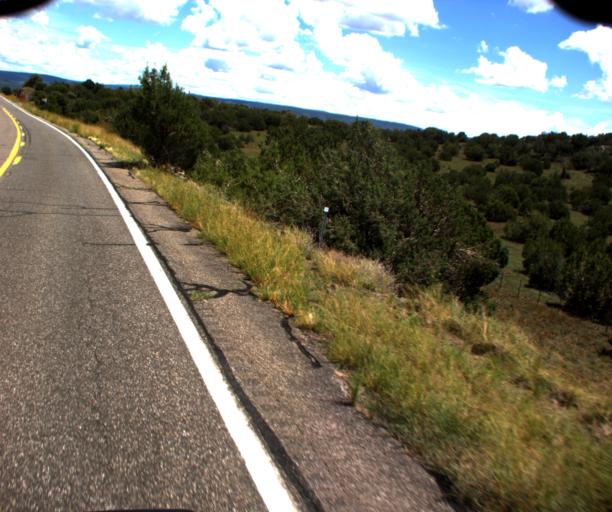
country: US
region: Arizona
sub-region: Gila County
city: Pine
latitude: 34.4859
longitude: -111.6193
